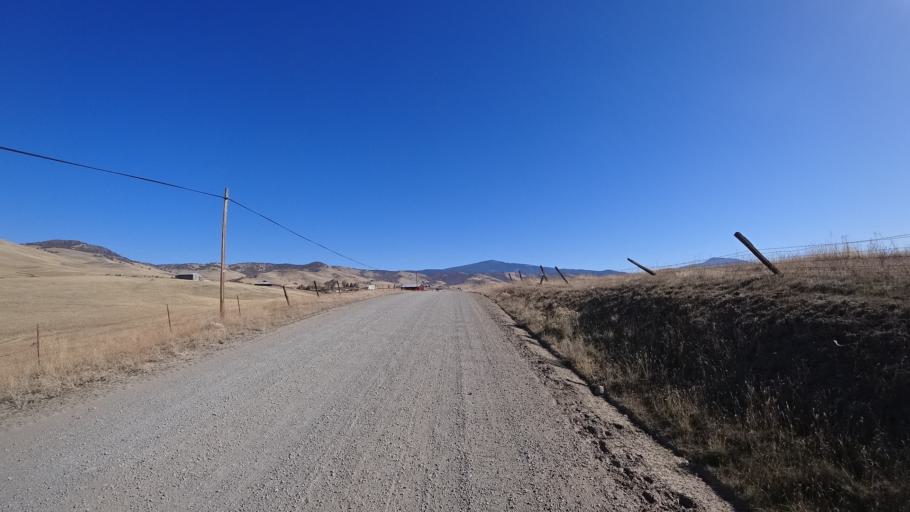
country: US
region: California
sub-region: Siskiyou County
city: Montague
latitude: 41.8298
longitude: -122.4006
